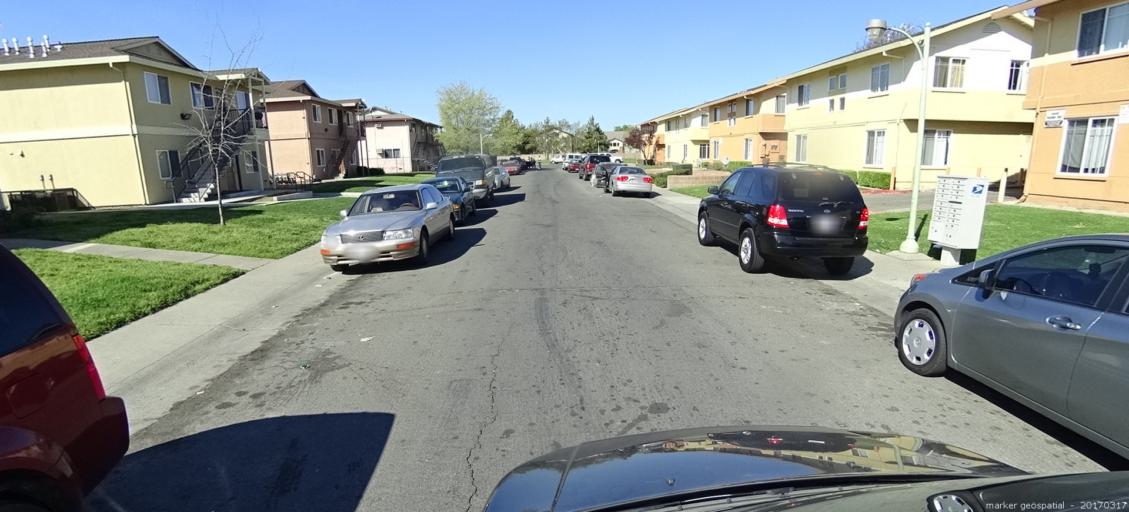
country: US
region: California
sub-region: Sacramento County
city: Parkway
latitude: 38.4824
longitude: -121.4756
